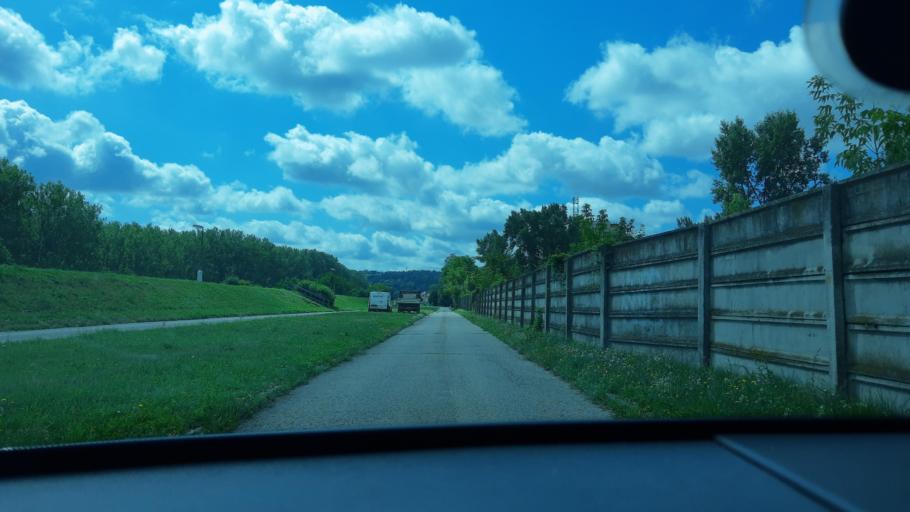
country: SK
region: Trnavsky
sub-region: Okres Trnava
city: Piestany
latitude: 48.5997
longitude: 17.8404
